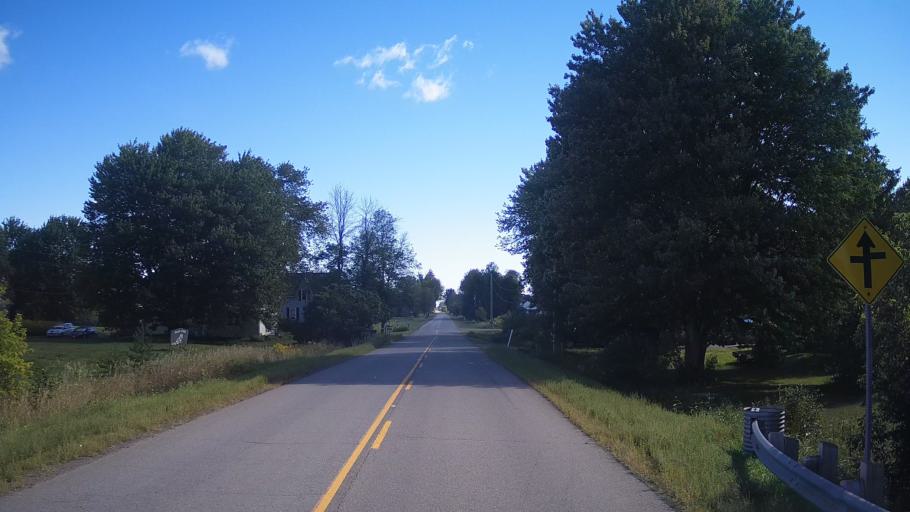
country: CA
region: Ontario
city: Prescott
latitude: 44.9119
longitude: -75.3750
